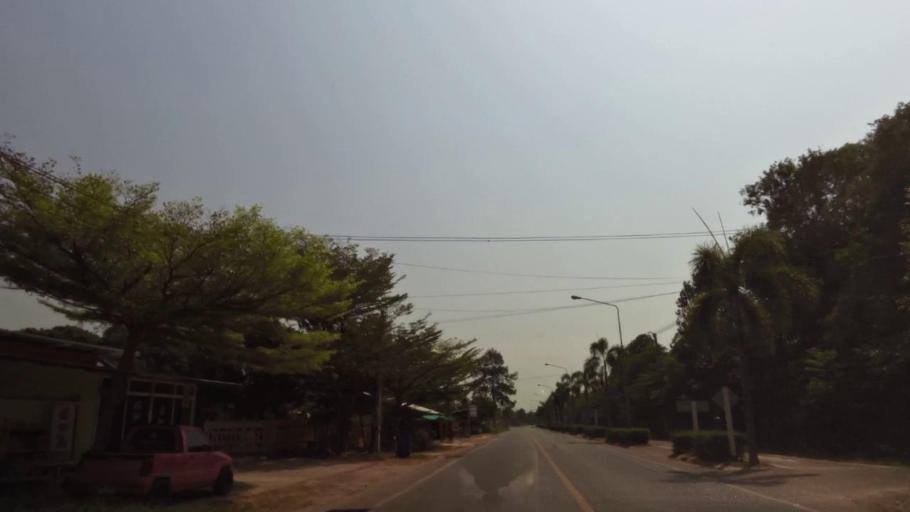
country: TH
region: Chanthaburi
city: Tha Mai
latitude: 12.5497
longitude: 101.9259
